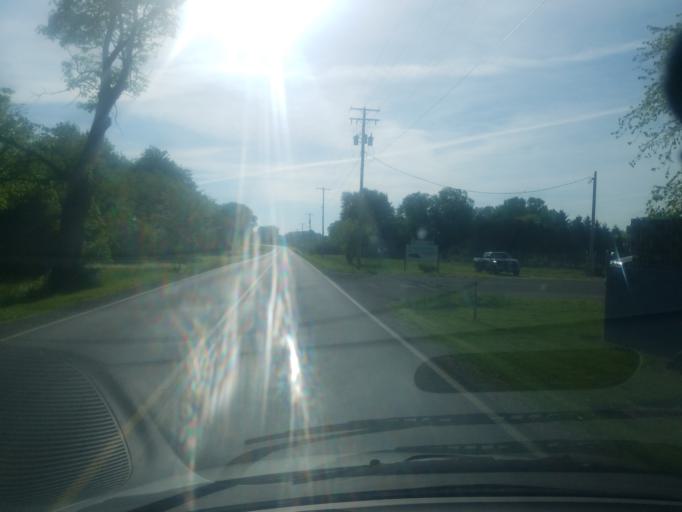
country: US
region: Ohio
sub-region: Marion County
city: Marion
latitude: 40.6000
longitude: -83.0942
